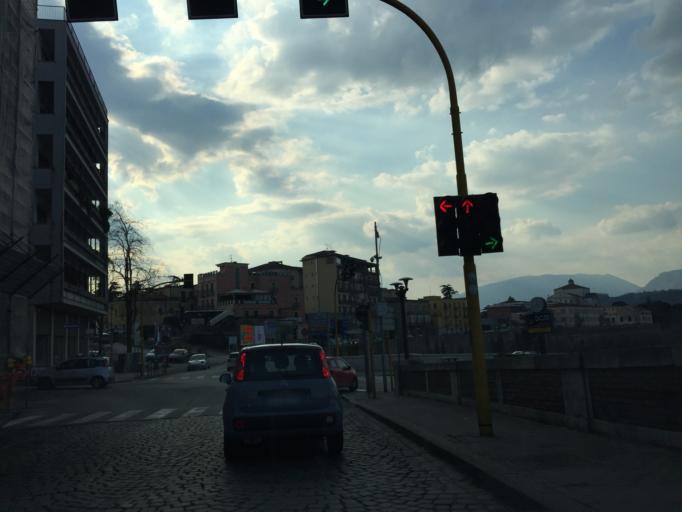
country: IT
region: Campania
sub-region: Provincia di Benevento
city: Benevento
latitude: 41.1334
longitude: 14.7741
